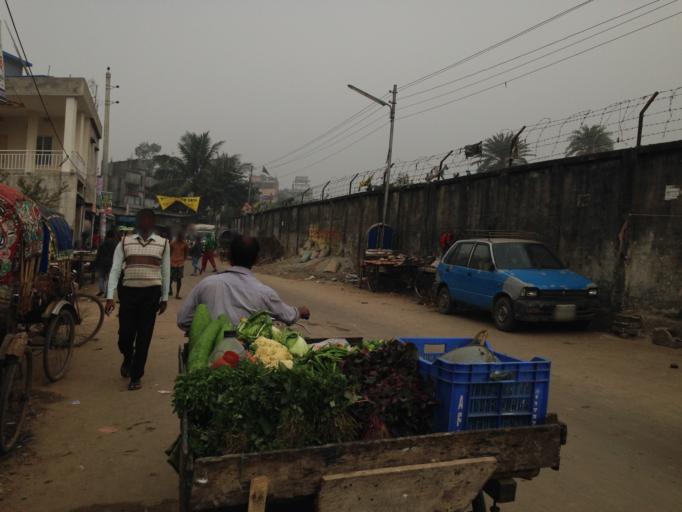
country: BD
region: Dhaka
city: Azimpur
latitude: 23.7953
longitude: 90.3430
